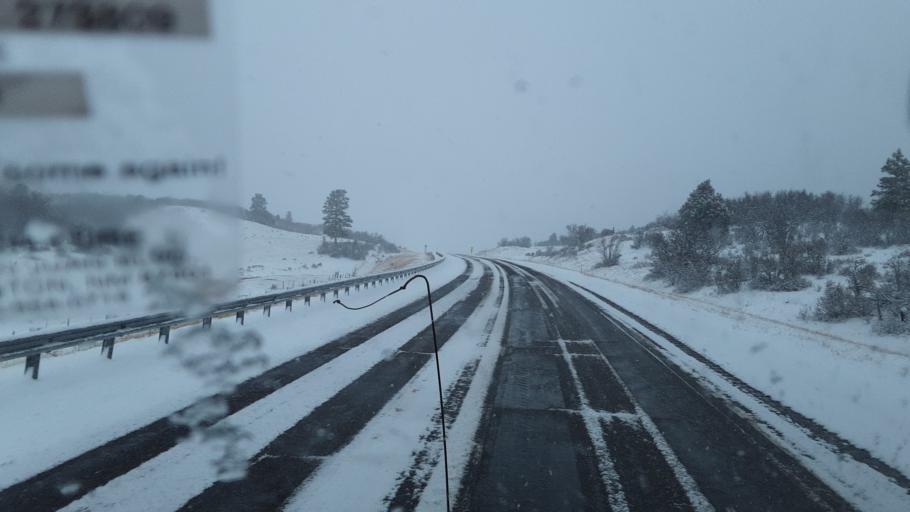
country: US
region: New Mexico
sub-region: Rio Arriba County
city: Chama
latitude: 36.9673
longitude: -106.7807
